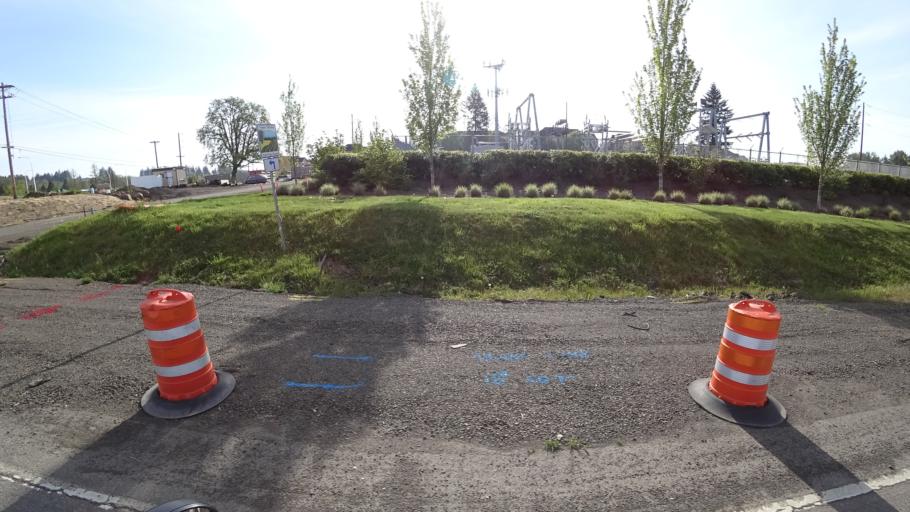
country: US
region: Oregon
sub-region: Washington County
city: King City
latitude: 45.4257
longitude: -122.8533
